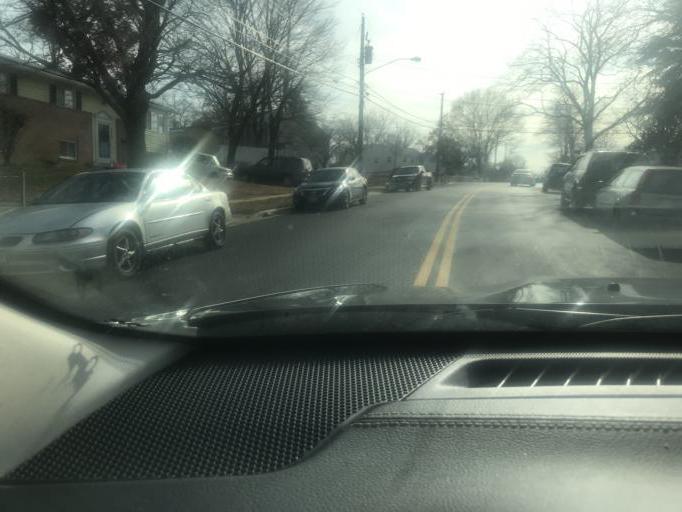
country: US
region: Maryland
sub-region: Prince George's County
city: Oxon Hill
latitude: 38.8115
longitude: -76.9837
